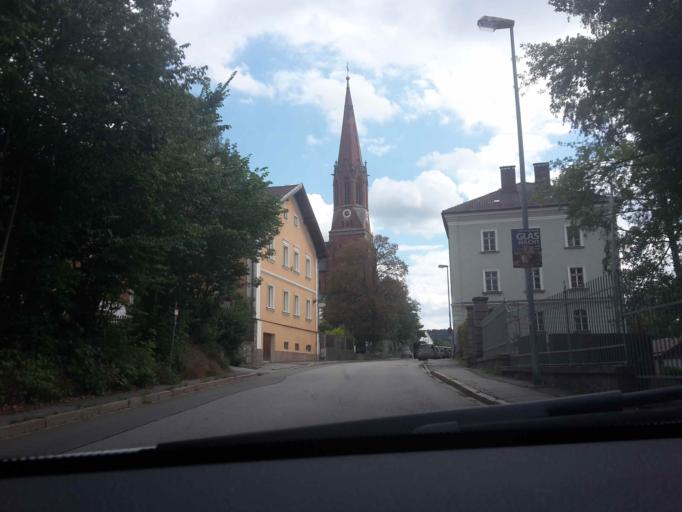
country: DE
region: Bavaria
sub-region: Lower Bavaria
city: Zwiesel
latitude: 49.0164
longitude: 13.2320
